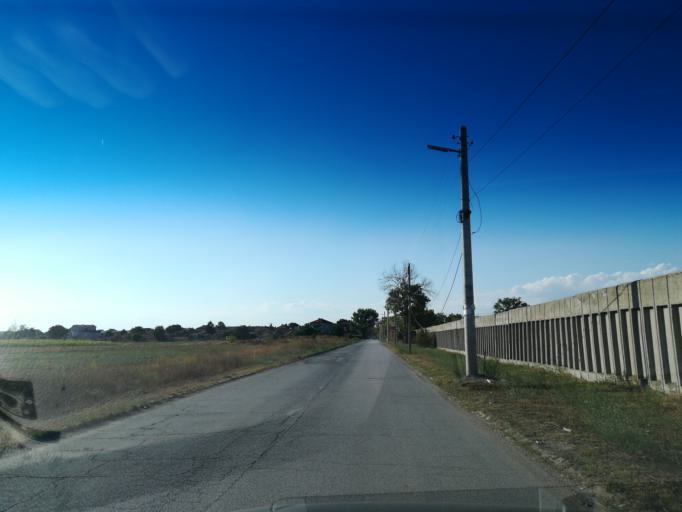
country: BG
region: Stara Zagora
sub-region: Obshtina Chirpan
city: Chirpan
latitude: 42.0926
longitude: 25.2363
